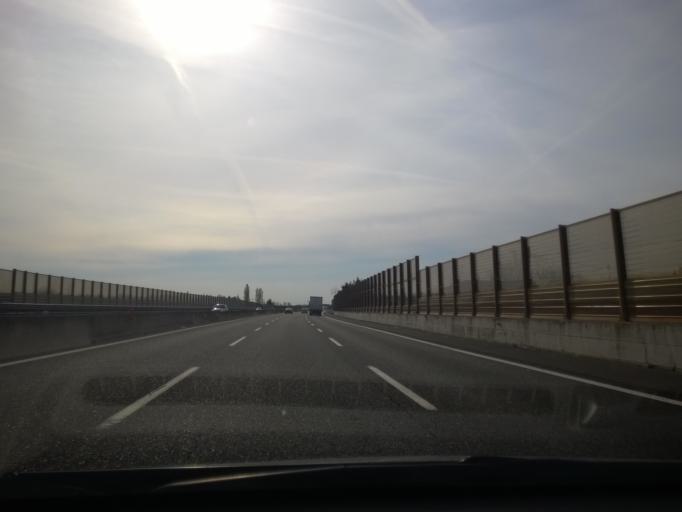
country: IT
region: Emilia-Romagna
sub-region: Forli-Cesena
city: Cesena
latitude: 44.1800
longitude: 12.2621
